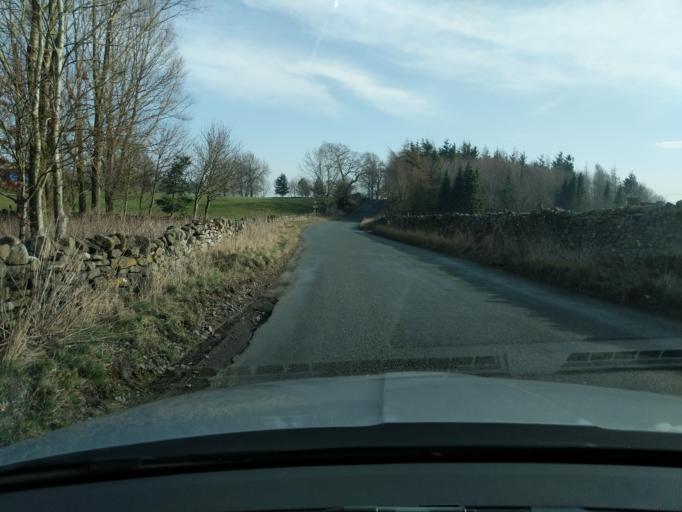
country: GB
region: England
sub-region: North Yorkshire
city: Leyburn
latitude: 54.3592
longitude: -1.8229
